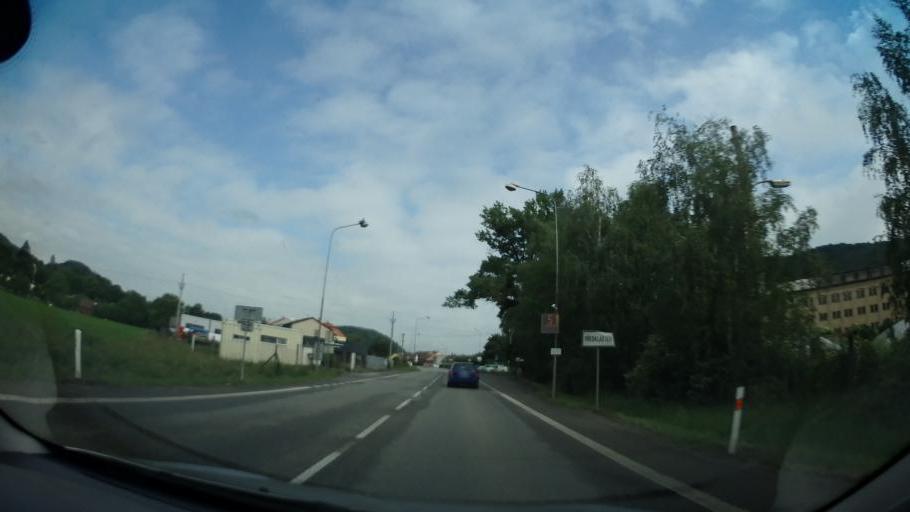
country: CZ
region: South Moravian
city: Predklasteri
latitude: 49.3507
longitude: 16.4087
